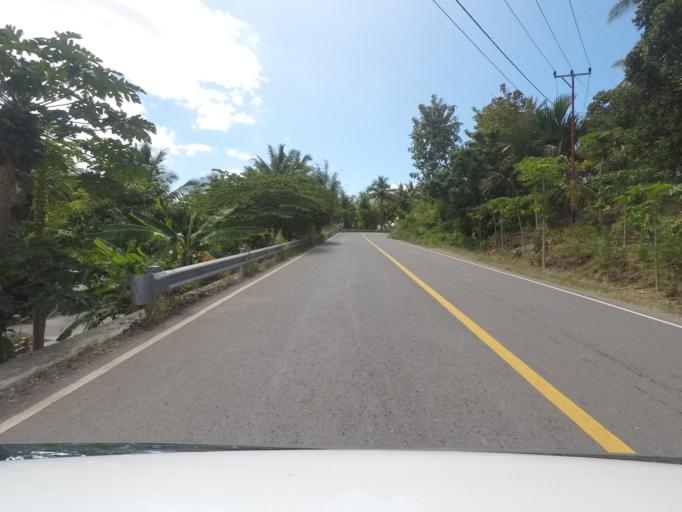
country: TL
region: Baucau
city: Baucau
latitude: -8.4903
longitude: 126.3544
